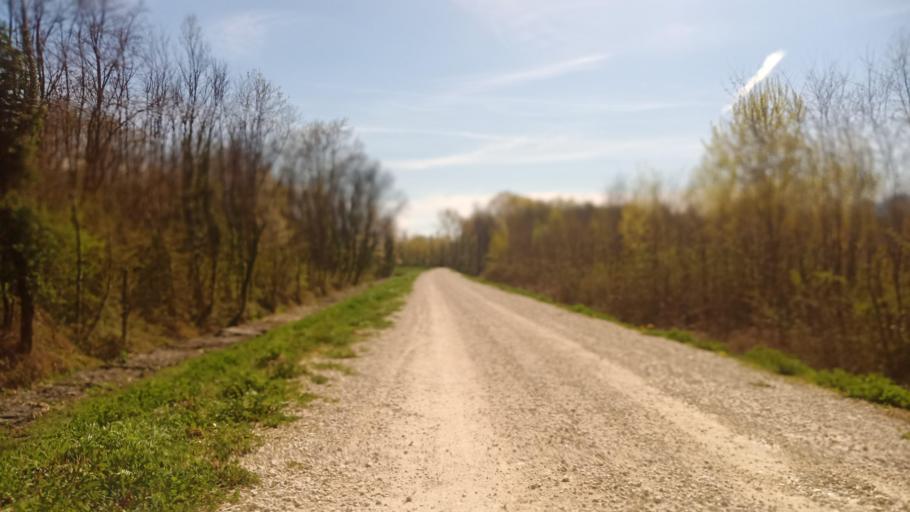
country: FR
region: Rhone-Alpes
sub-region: Departement de l'Isere
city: Tencin
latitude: 45.3146
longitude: 5.9451
